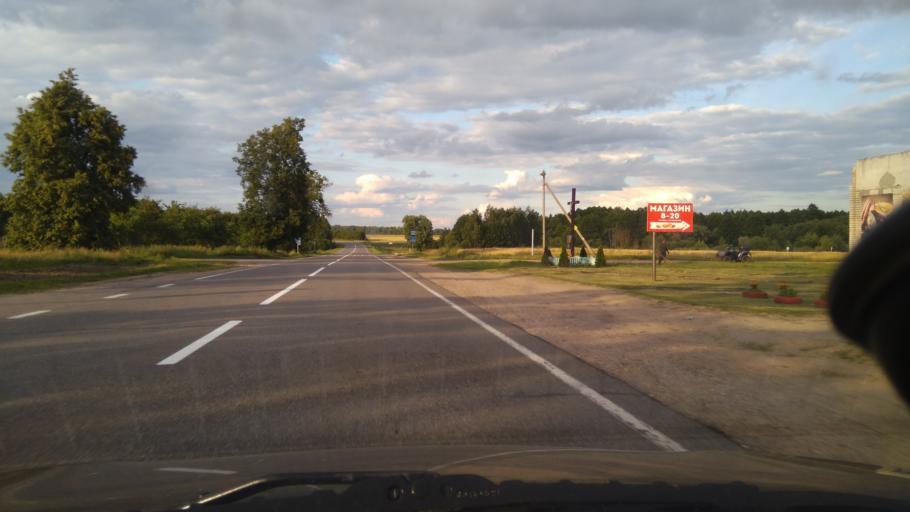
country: BY
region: Grodnenskaya
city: Shchuchin
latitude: 53.5136
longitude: 24.6928
